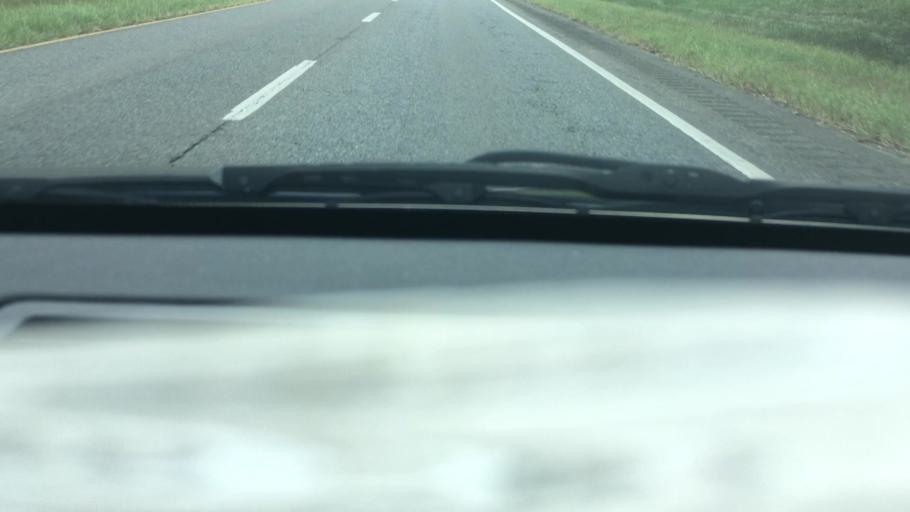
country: US
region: Alabama
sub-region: Pickens County
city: Gordo
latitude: 33.2811
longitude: -87.8009
